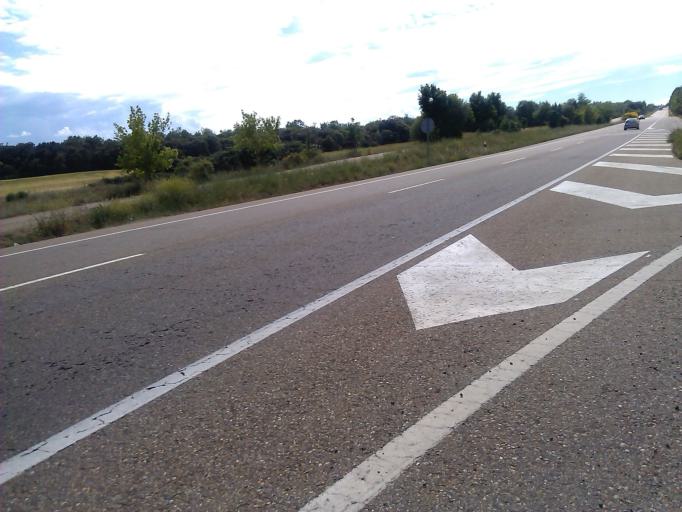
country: ES
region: Castille and Leon
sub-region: Provincia de Leon
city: San Justo de la Vega
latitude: 42.4477
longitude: -5.9656
